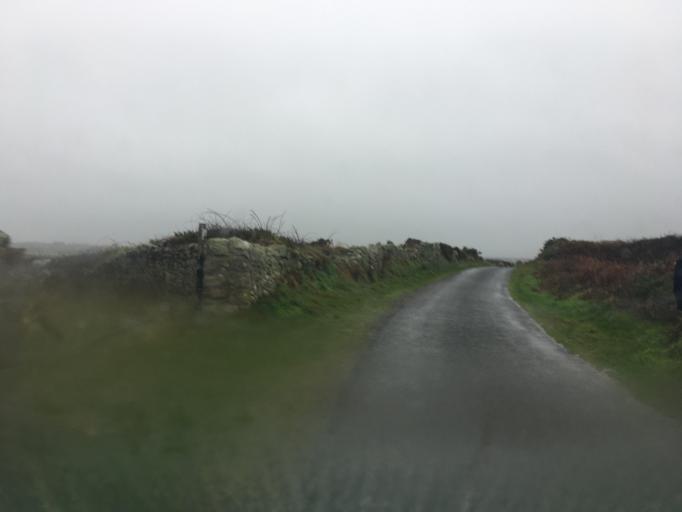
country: FR
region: Lower Normandy
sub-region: Departement de la Manche
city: Beaumont-Hague
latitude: 49.7253
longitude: -1.9234
